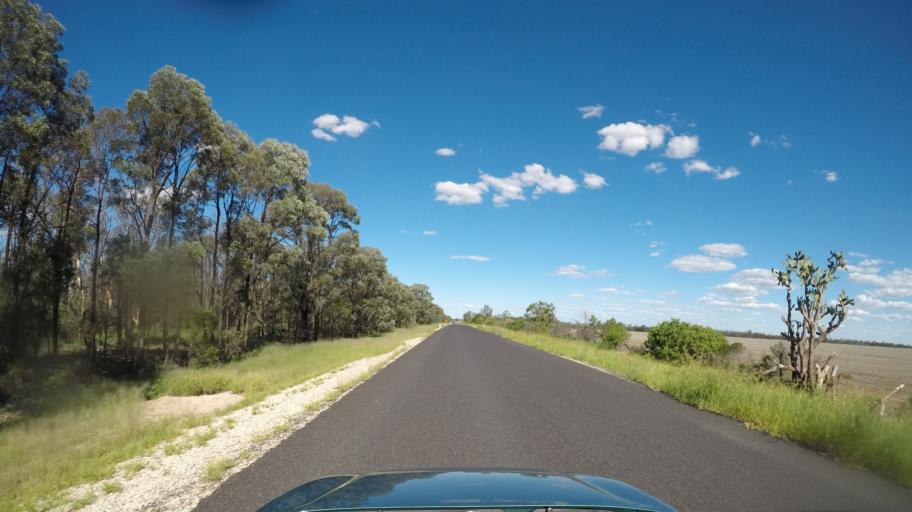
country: AU
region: Queensland
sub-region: Goondiwindi
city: Goondiwindi
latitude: -28.1611
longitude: 150.4090
